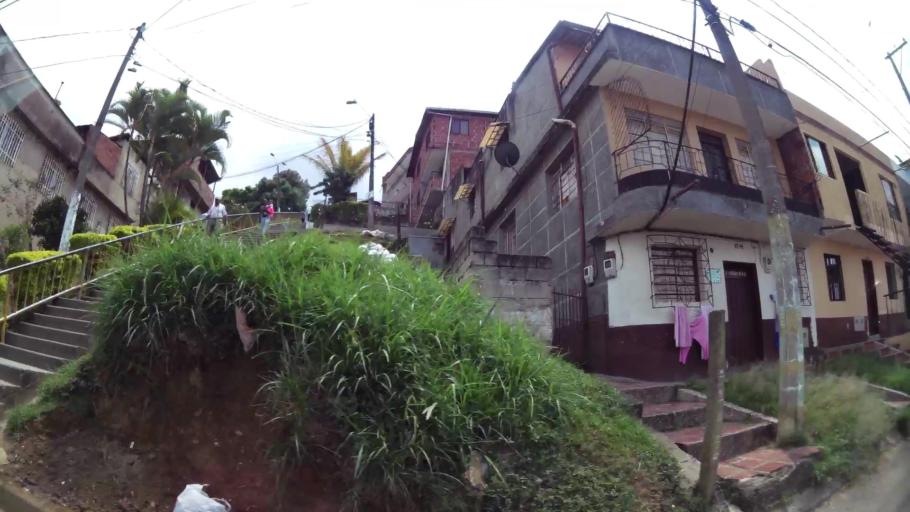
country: CO
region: Antioquia
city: Medellin
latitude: 6.2645
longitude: -75.5471
